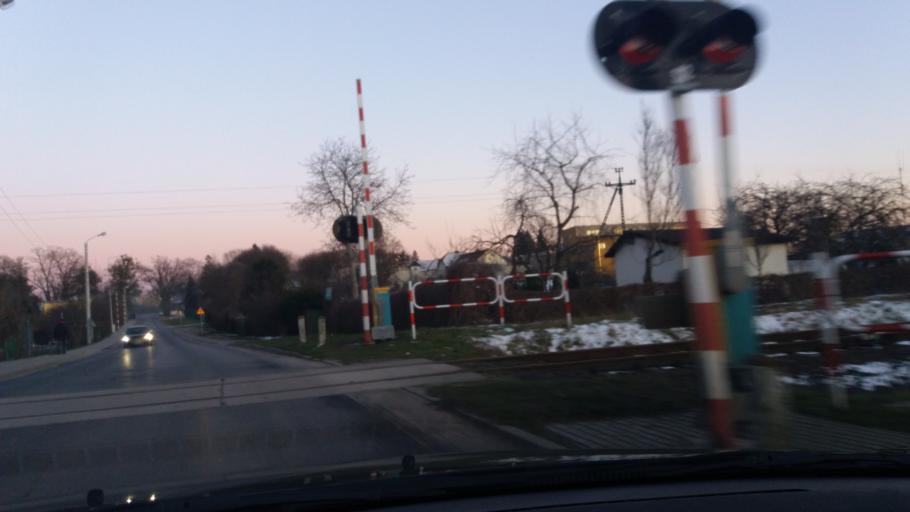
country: PL
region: Warmian-Masurian Voivodeship
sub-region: Powiat szczycienski
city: Szczytno
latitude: 53.5599
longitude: 20.9831
